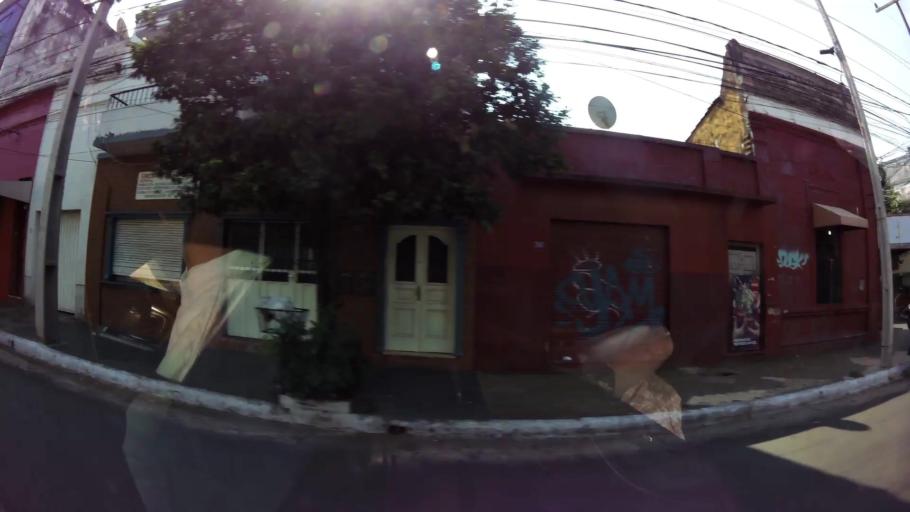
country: PY
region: Asuncion
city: Asuncion
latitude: -25.2920
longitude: -57.6295
